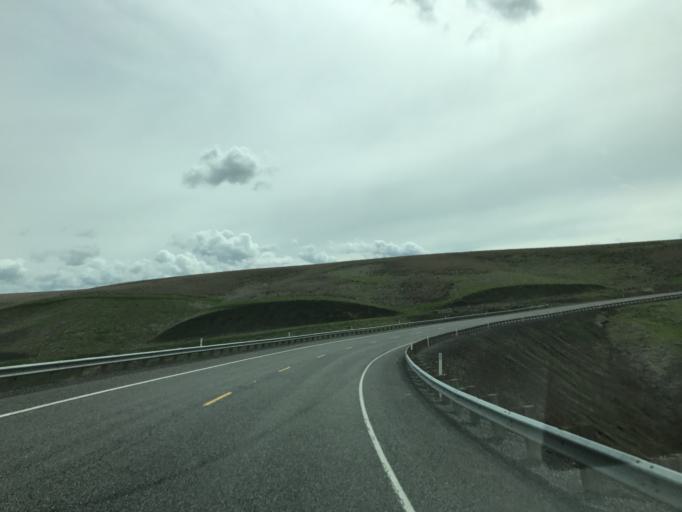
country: US
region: Washington
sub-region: Garfield County
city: Pomeroy
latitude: 46.5269
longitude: -117.7865
